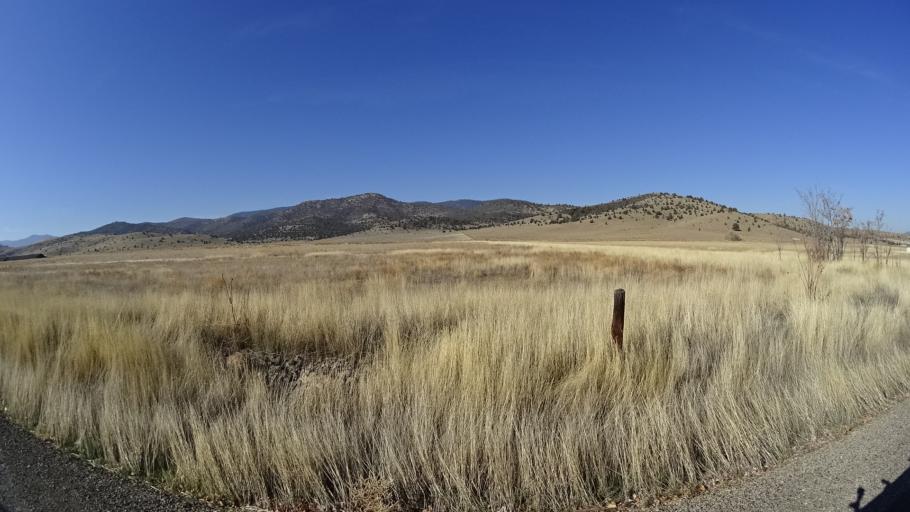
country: US
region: California
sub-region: Siskiyou County
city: Montague
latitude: 41.6217
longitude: -122.5298
